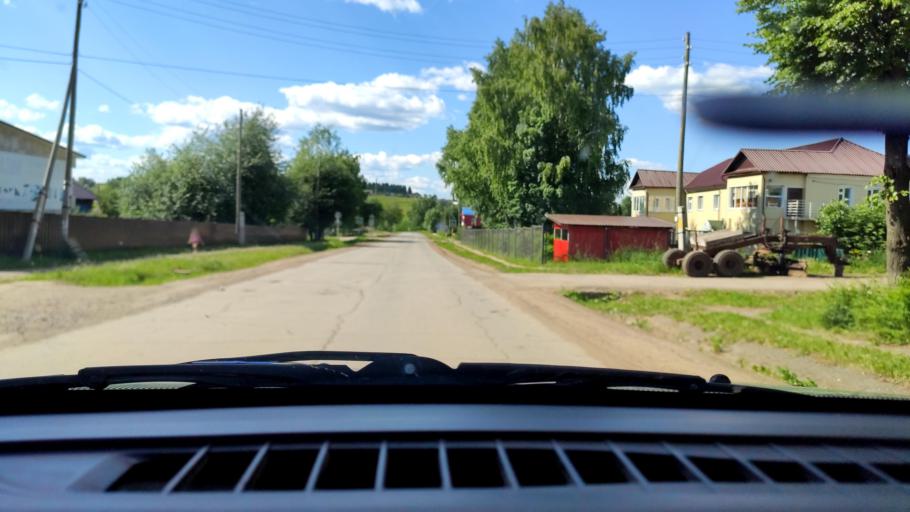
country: RU
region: Perm
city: Uinskoye
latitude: 57.1156
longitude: 56.5272
